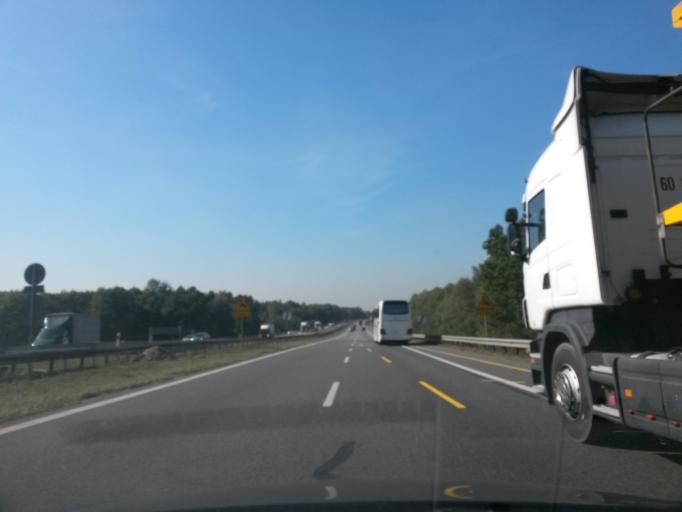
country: PL
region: Silesian Voivodeship
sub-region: Myslowice
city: Myslowice
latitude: 50.2184
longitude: 19.1160
